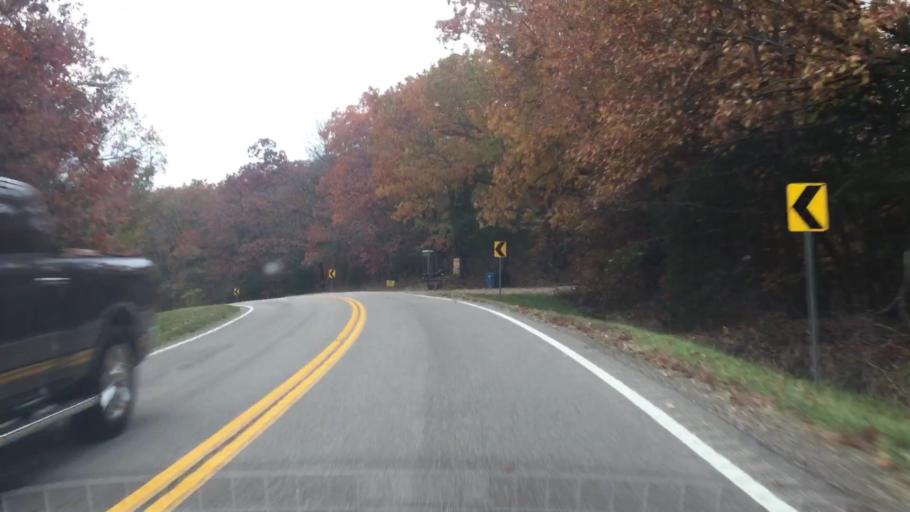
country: US
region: Missouri
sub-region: Gasconade County
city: Hermann
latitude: 38.7206
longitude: -91.6719
